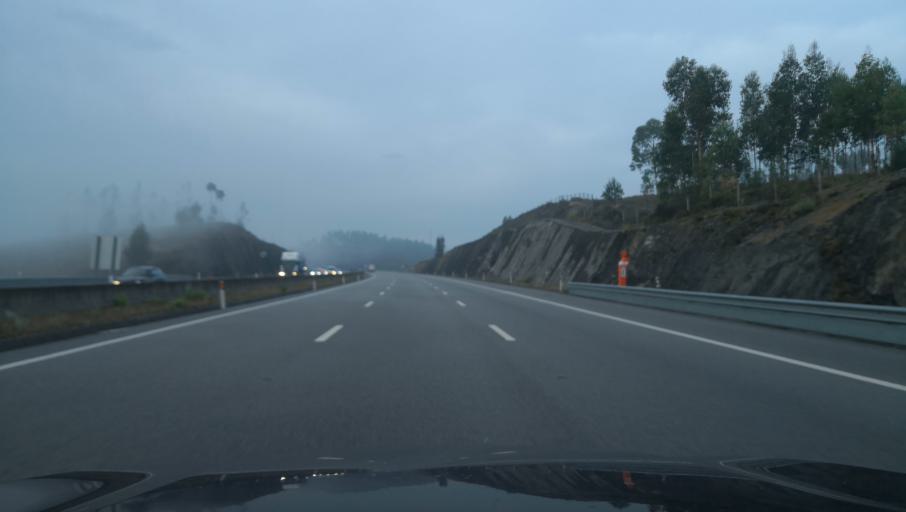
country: PT
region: Porto
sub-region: Paredes
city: Recarei
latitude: 41.1313
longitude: -8.4288
